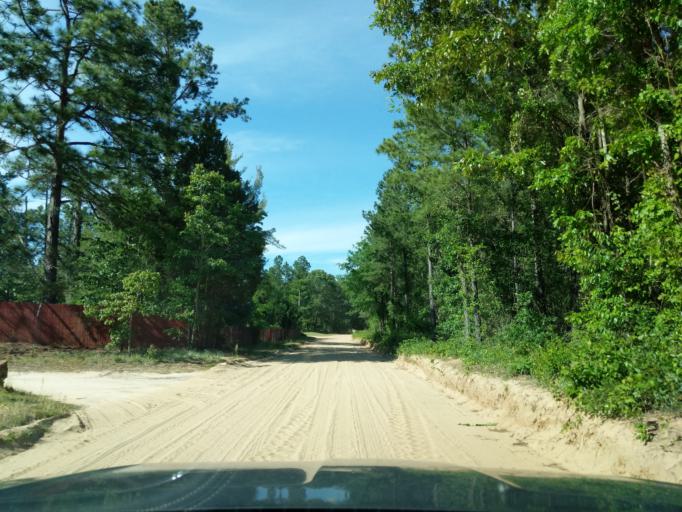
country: US
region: Georgia
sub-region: Jefferson County
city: Wrens
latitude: 33.2201
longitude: -82.3554
